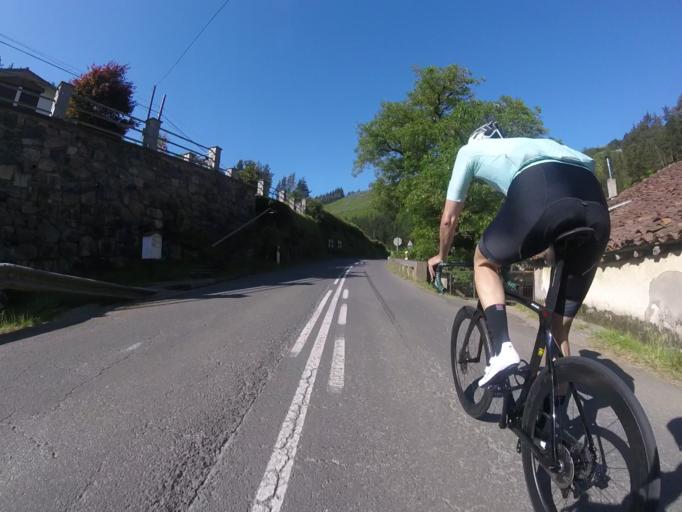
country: ES
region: Basque Country
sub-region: Provincia de Guipuzcoa
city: Beizama
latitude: 43.1427
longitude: -2.2350
